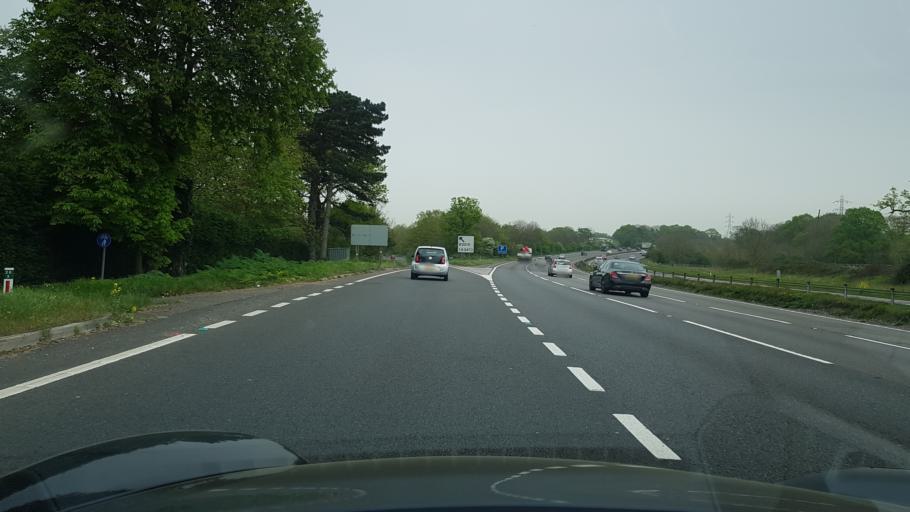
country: GB
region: England
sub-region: Surrey
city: Send
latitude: 51.2747
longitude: -0.5244
